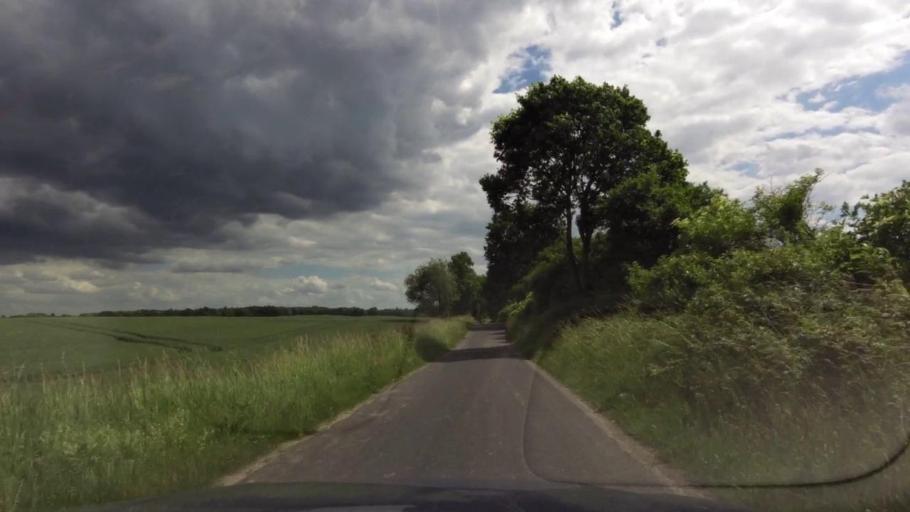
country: PL
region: West Pomeranian Voivodeship
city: Trzcinsko Zdroj
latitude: 52.9066
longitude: 14.6036
